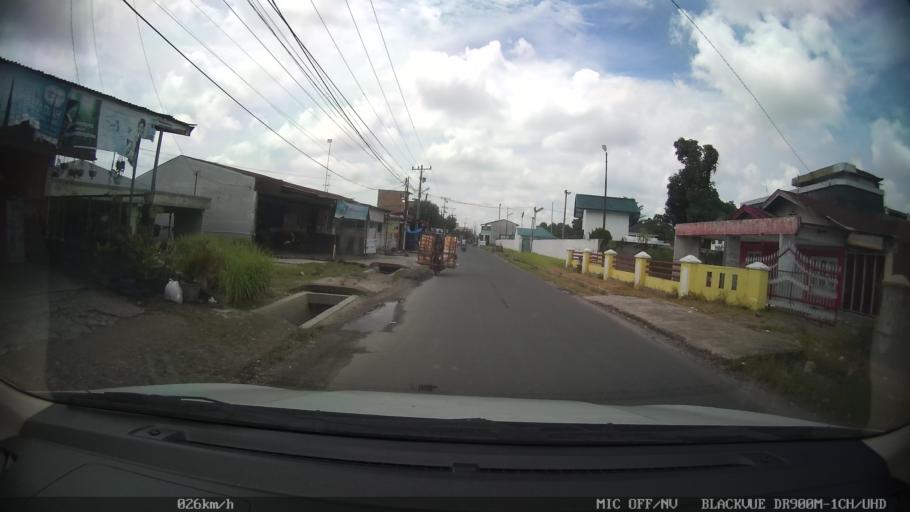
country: ID
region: North Sumatra
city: Medan
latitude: 3.6080
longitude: 98.7475
